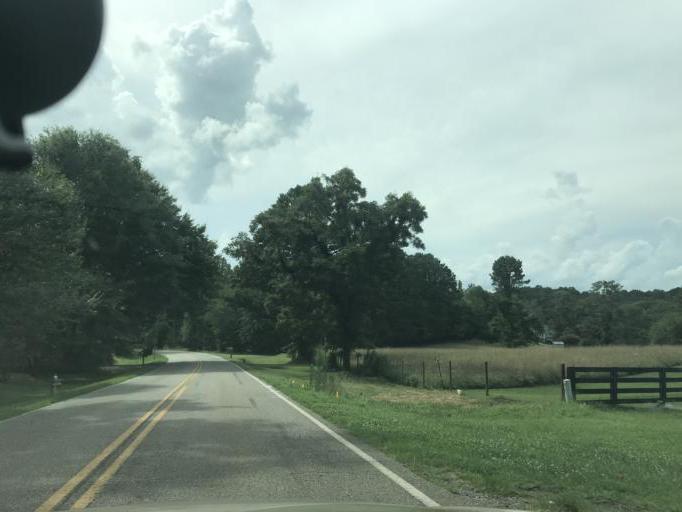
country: US
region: Georgia
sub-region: Forsyth County
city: Cumming
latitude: 34.2875
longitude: -84.2394
